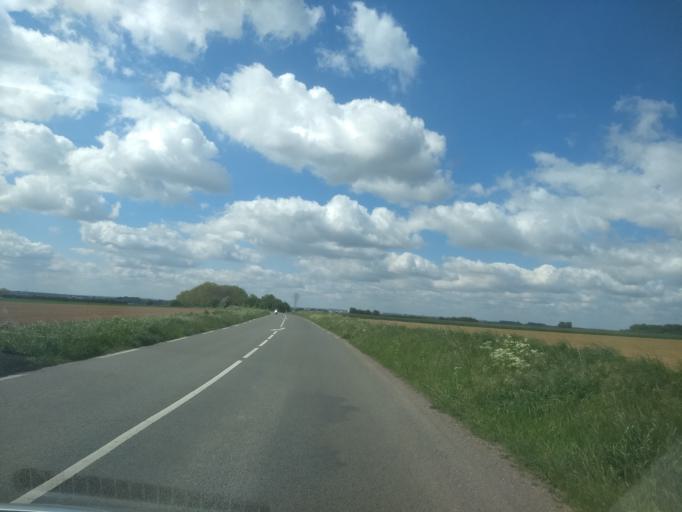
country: FR
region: Nord-Pas-de-Calais
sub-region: Departement du Pas-de-Calais
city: Bailleul-Sir-Berthoult
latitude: 50.3321
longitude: 2.8334
